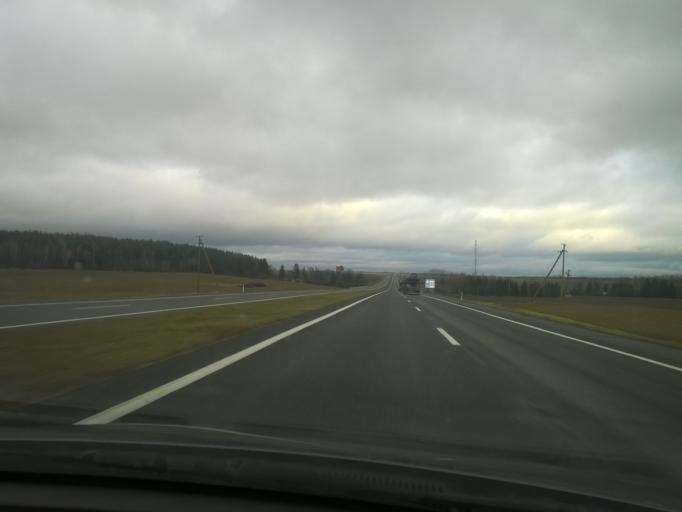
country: BY
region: Minsk
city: Snow
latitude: 53.2923
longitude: 26.3487
